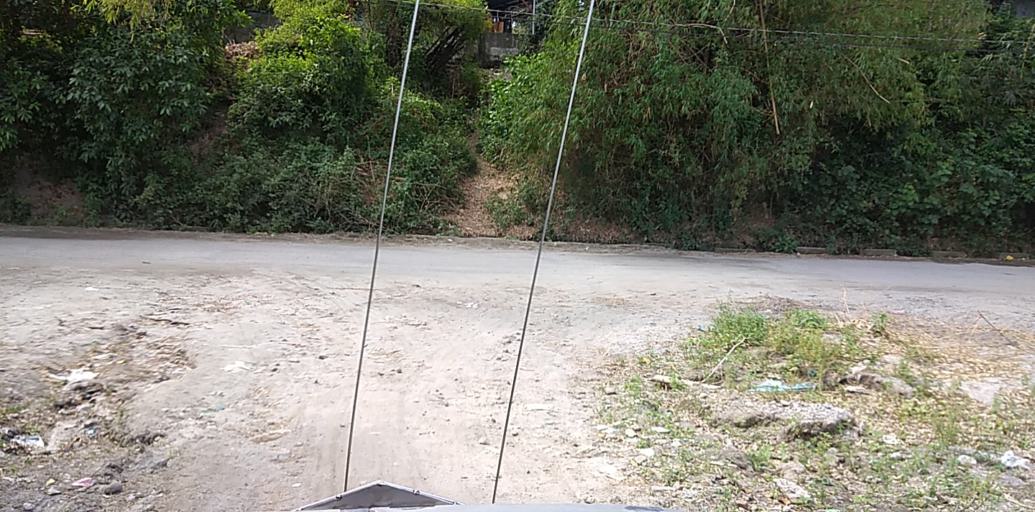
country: PH
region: Central Luzon
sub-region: Province of Pampanga
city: Porac
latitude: 15.0775
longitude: 120.5334
